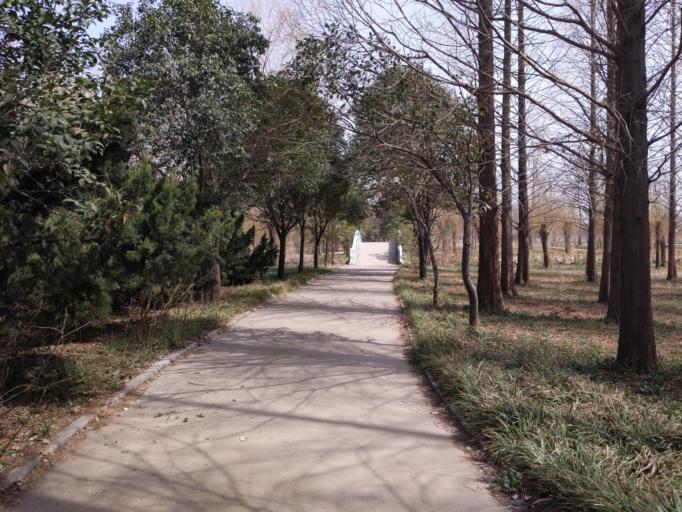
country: CN
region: Henan Sheng
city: Puyang
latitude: 35.7793
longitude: 114.9453
